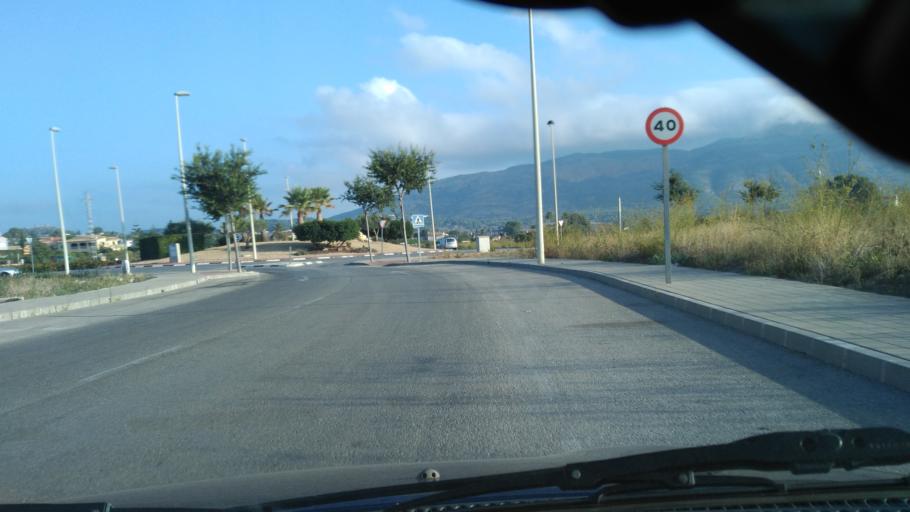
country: ES
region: Valencia
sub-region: Provincia de Alicante
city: Gata de Gorgos
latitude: 38.7787
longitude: 0.0871
